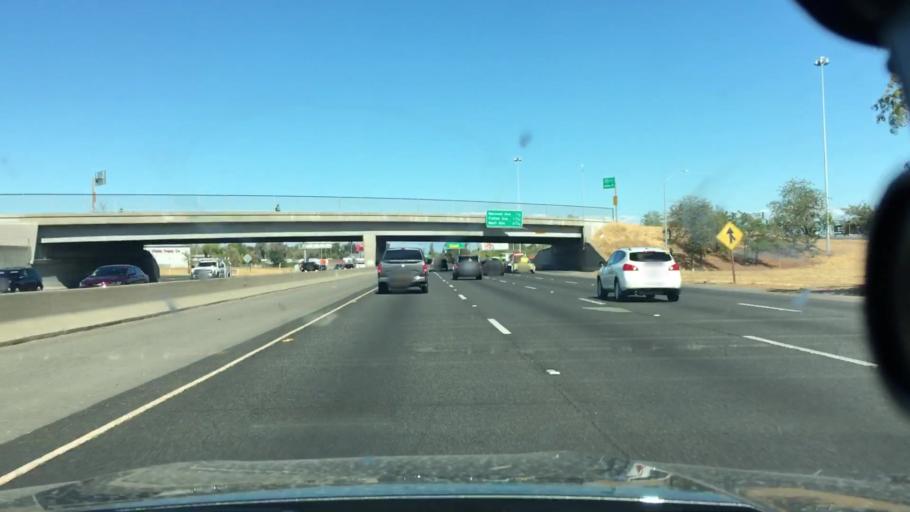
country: US
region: California
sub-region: Sacramento County
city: Arden-Arcade
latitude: 38.6103
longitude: -121.4274
